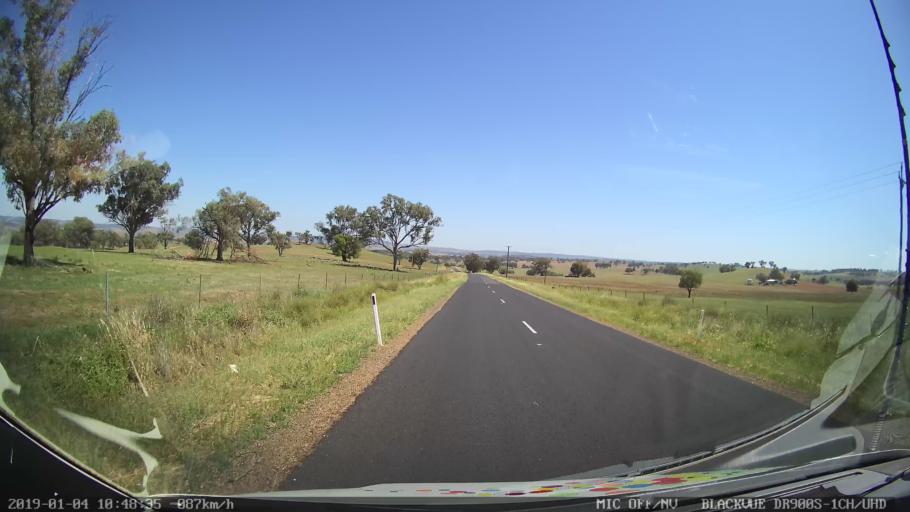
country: AU
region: New South Wales
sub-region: Cabonne
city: Molong
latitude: -33.2581
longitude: 148.7124
